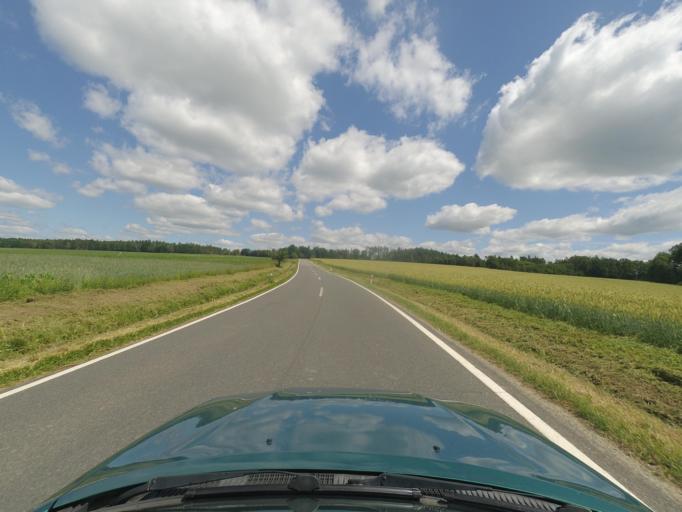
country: CZ
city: Dobruska
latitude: 50.3122
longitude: 16.1932
